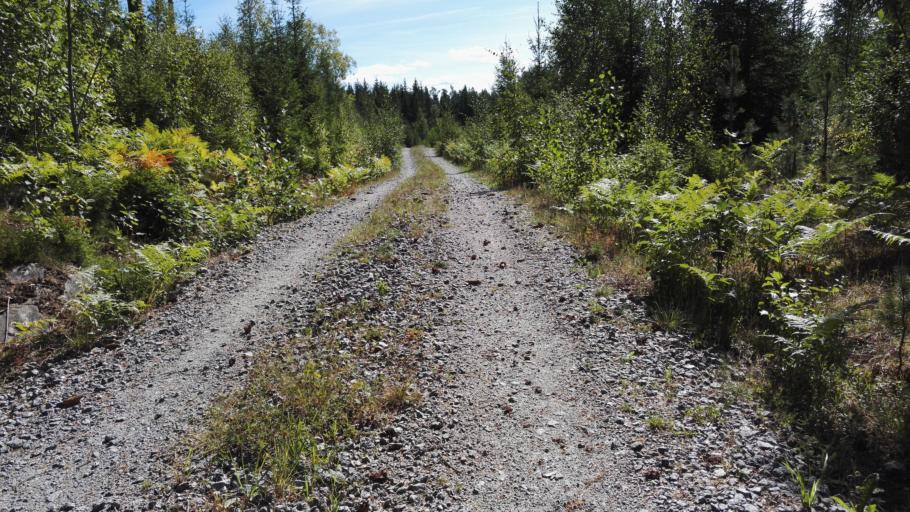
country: SE
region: Joenkoeping
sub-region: Vetlanda Kommun
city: Landsbro
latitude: 57.3239
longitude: 14.8567
